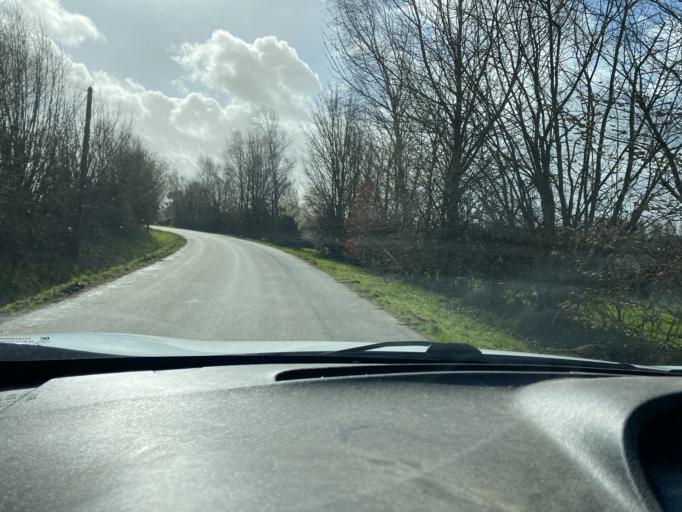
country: FR
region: Brittany
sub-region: Departement d'Ille-et-Vilaine
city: Melesse
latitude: 48.2100
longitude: -1.6921
